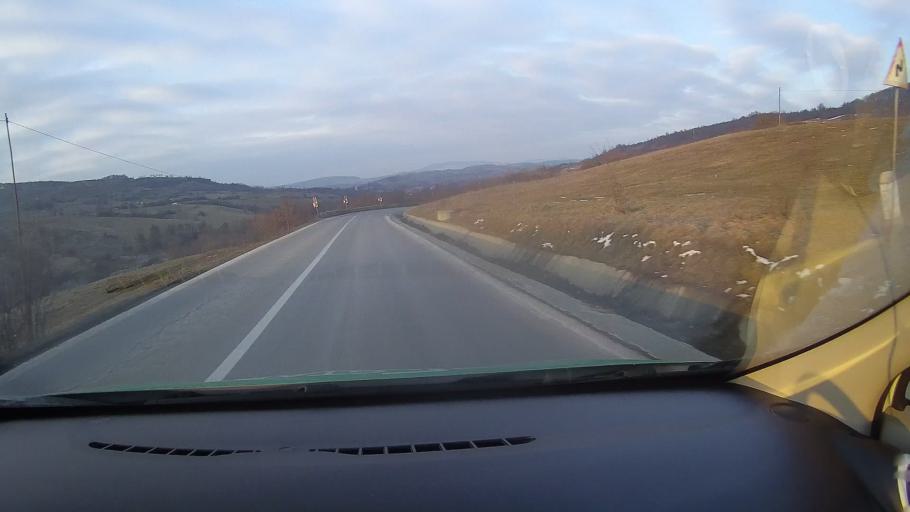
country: RO
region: Harghita
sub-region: Comuna Simonesti
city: Simonesti
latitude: 46.3217
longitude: 25.0995
